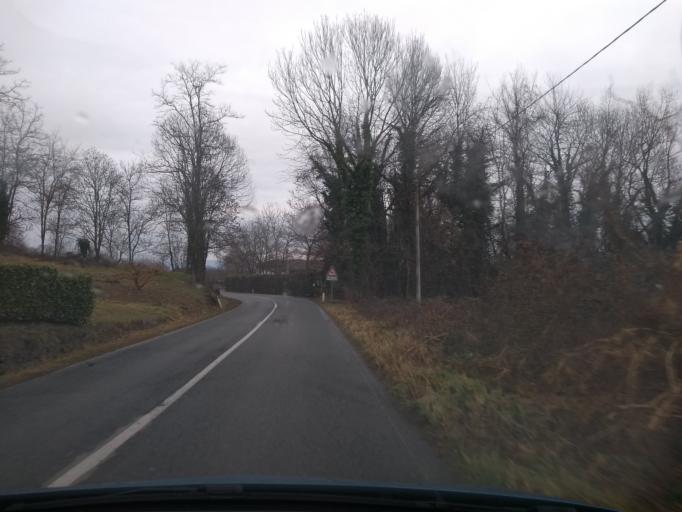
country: IT
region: Piedmont
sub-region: Provincia di Torino
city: Strambinello
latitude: 45.4220
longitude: 7.7709
